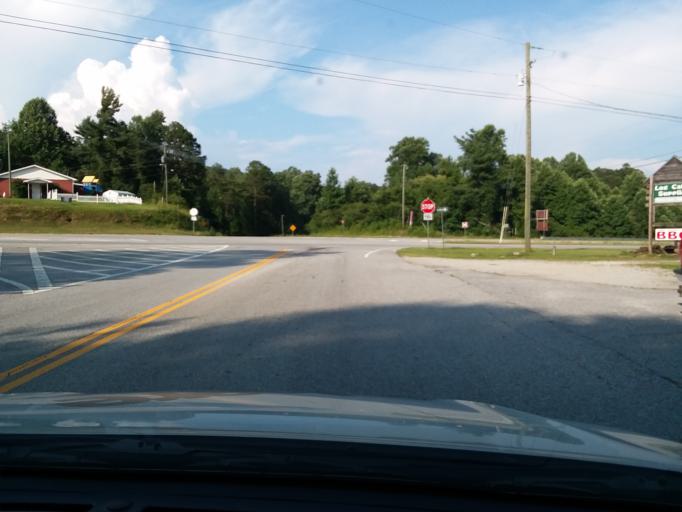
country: US
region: Georgia
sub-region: Rabun County
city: Clayton
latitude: 34.7985
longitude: -83.4200
